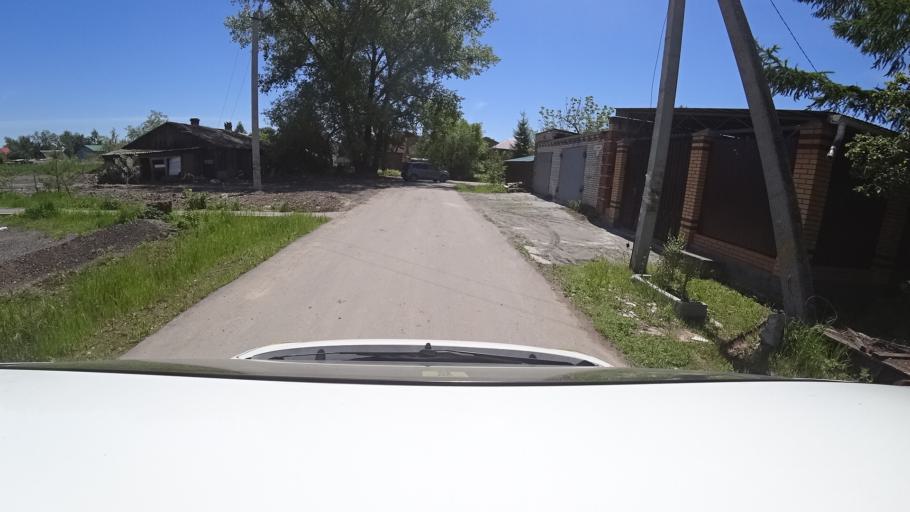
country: RU
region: Khabarovsk Krai
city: Topolevo
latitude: 48.5091
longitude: 135.1765
